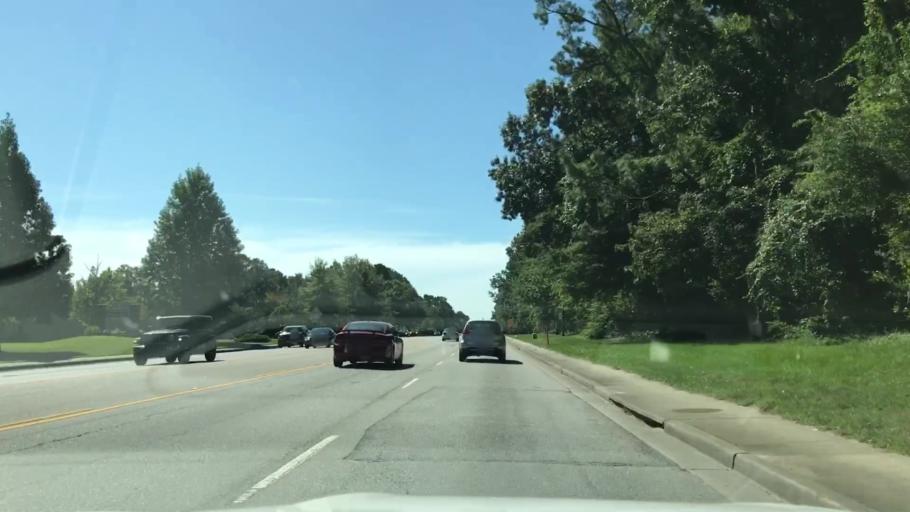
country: US
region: South Carolina
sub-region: Berkeley County
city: Goose Creek
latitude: 33.0294
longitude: -80.0583
